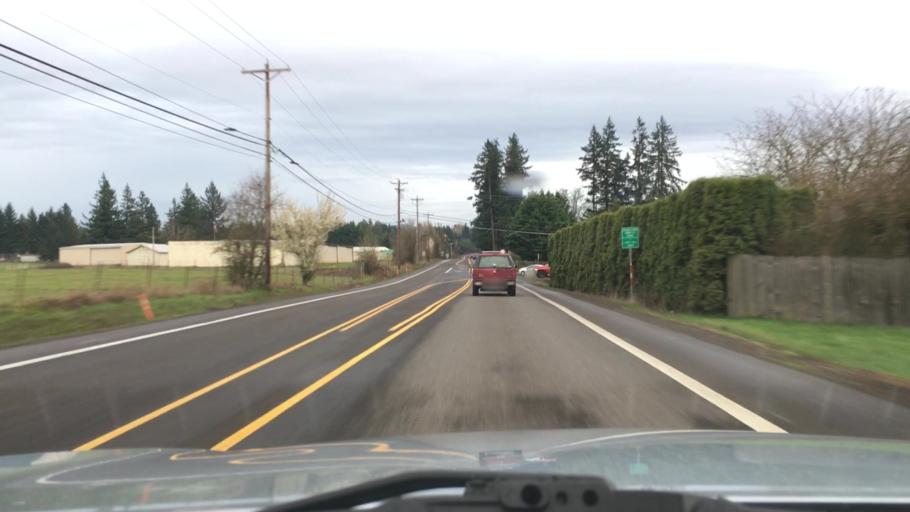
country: US
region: Oregon
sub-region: Clackamas County
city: Beavercreek
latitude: 45.3177
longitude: -122.5555
